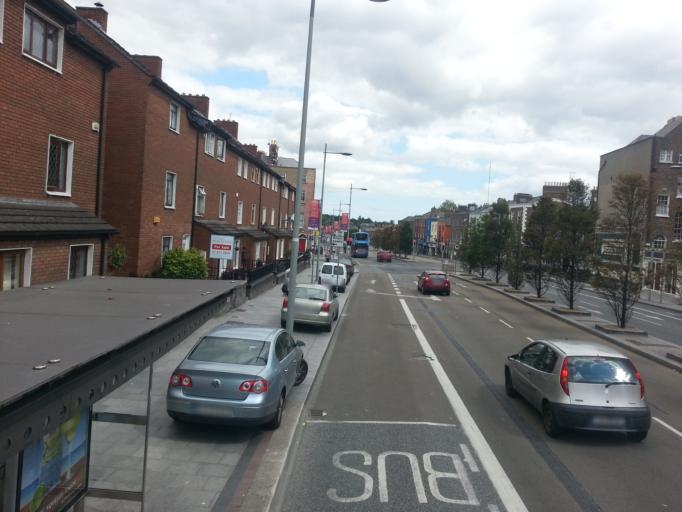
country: IE
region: Leinster
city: Drumcondra
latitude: 53.3585
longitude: -6.2628
